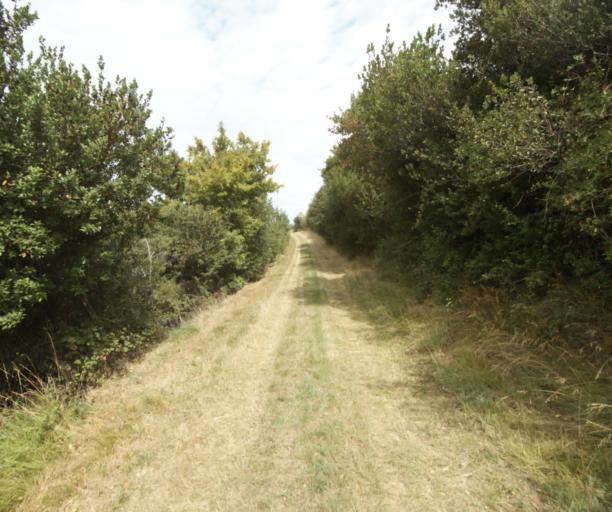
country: FR
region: Midi-Pyrenees
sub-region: Departement de la Haute-Garonne
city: Saint-Felix-Lauragais
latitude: 43.4460
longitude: 1.9007
